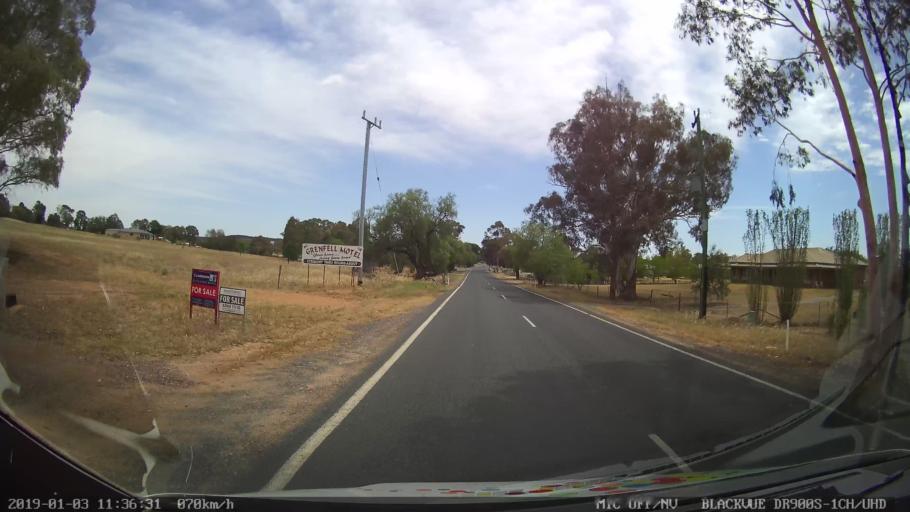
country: AU
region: New South Wales
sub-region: Weddin
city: Grenfell
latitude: -33.9099
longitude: 148.1598
